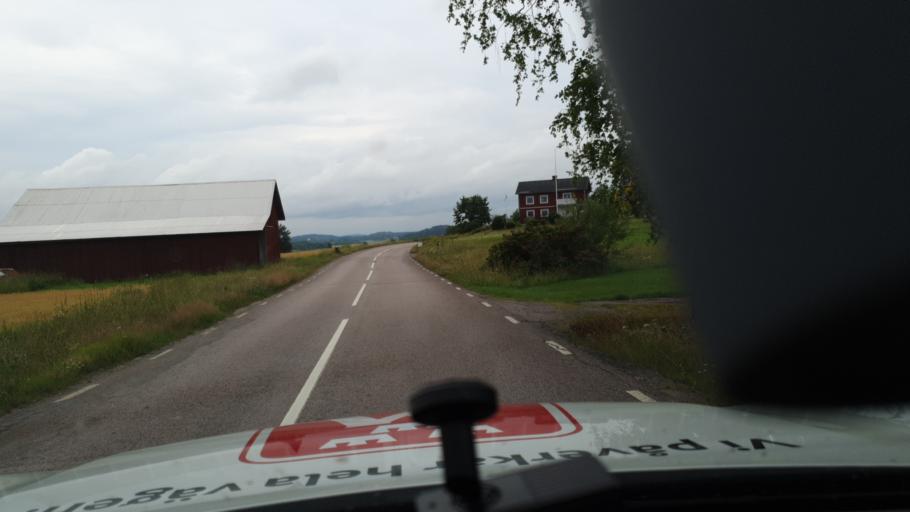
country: SE
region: Vaermland
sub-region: Sunne Kommun
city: Sunne
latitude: 59.7663
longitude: 13.2387
